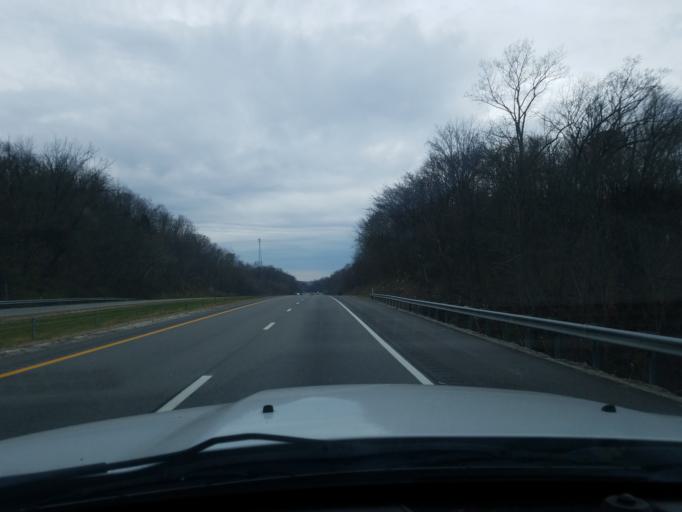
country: US
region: Ohio
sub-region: Lawrence County
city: Burlington
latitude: 38.3949
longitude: -82.5244
